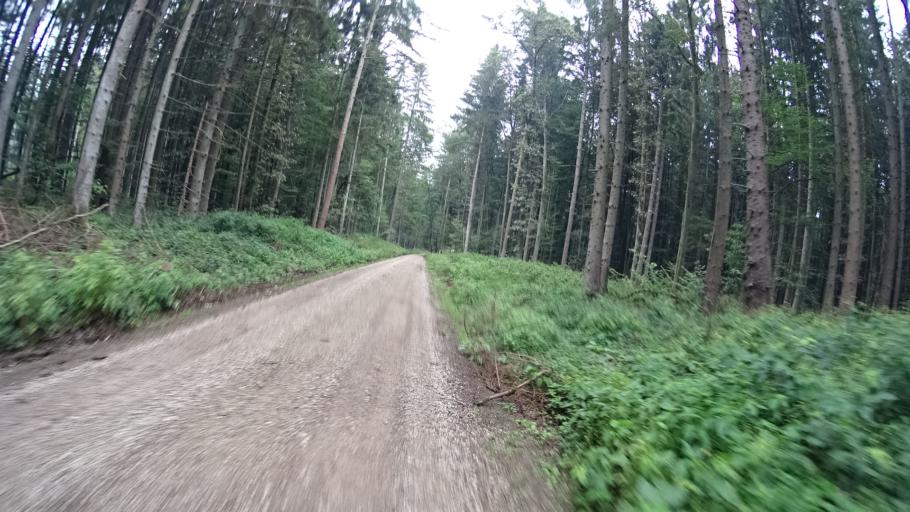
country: DE
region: Bavaria
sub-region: Upper Bavaria
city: Stammham
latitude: 48.8536
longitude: 11.4940
